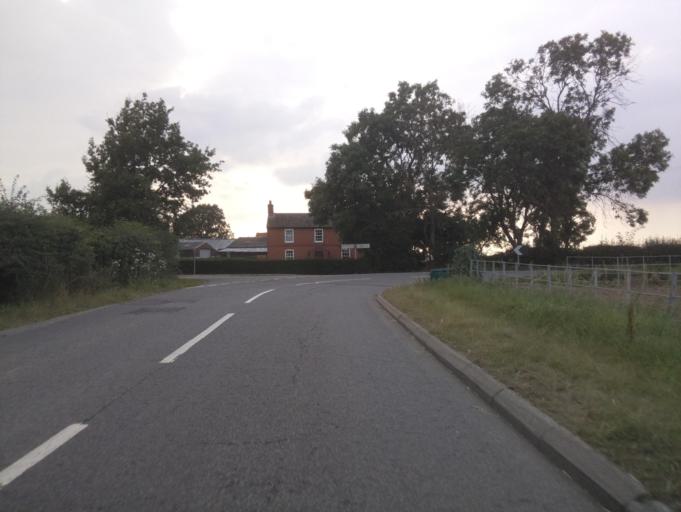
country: GB
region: England
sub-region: Lincolnshire
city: Skellingthorpe
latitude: 53.1343
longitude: -0.6463
